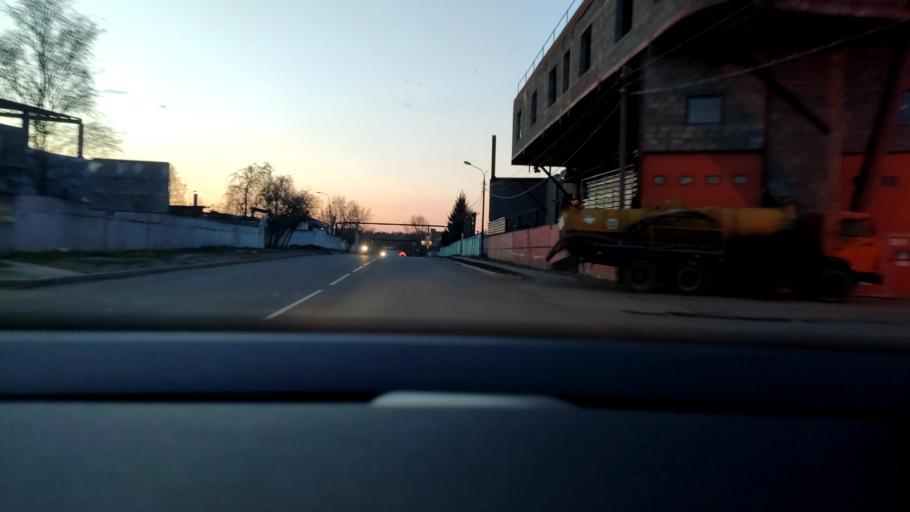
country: RU
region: Moskovskaya
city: Reutov
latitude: 55.7684
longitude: 37.8801
